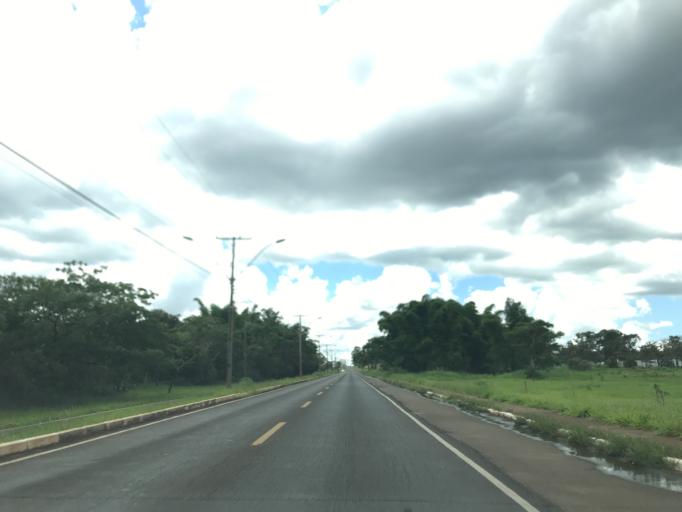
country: BR
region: Federal District
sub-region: Brasilia
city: Brasilia
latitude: -15.8984
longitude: -47.9303
